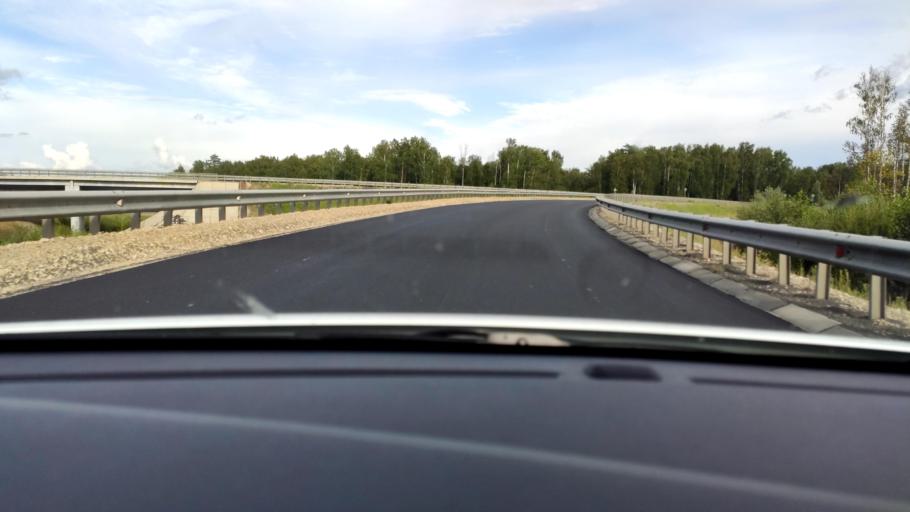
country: RU
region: Mariy-El
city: Yoshkar-Ola
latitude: 56.5686
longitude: 47.9134
